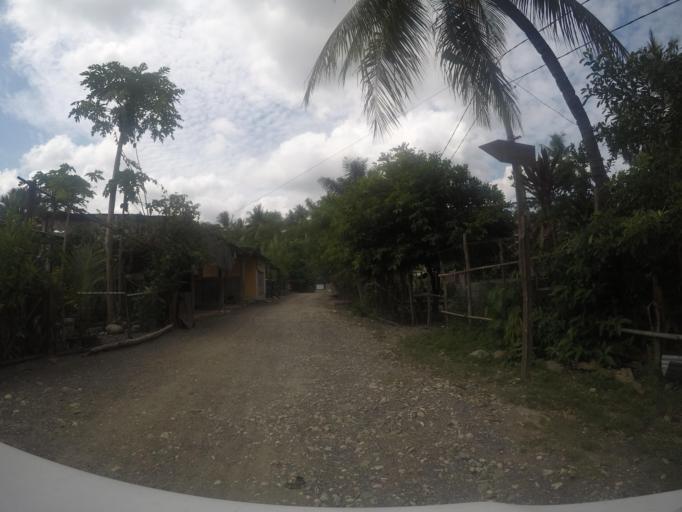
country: TL
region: Viqueque
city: Viqueque
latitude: -8.8605
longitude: 126.3628
